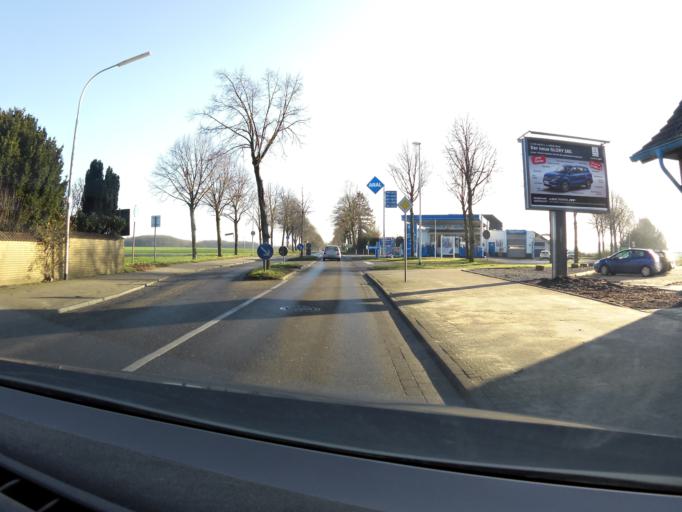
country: NL
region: Limburg
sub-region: Gemeente Venlo
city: Venlo
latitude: 51.3115
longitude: 6.2046
